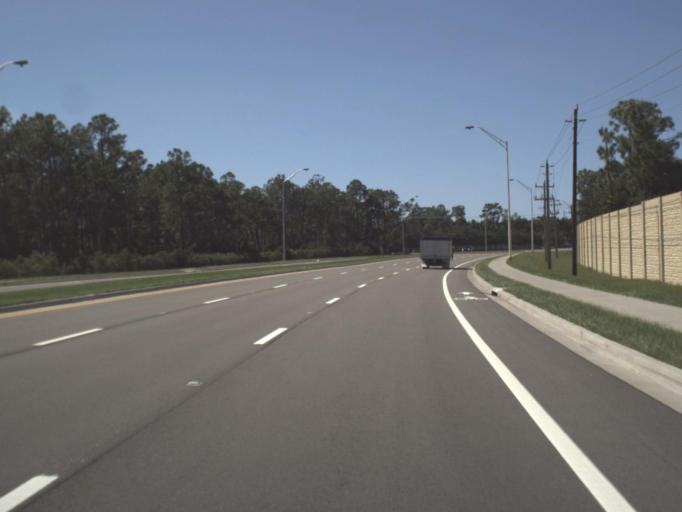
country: US
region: Florida
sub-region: Collier County
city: Lely
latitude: 26.1405
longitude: -81.7081
